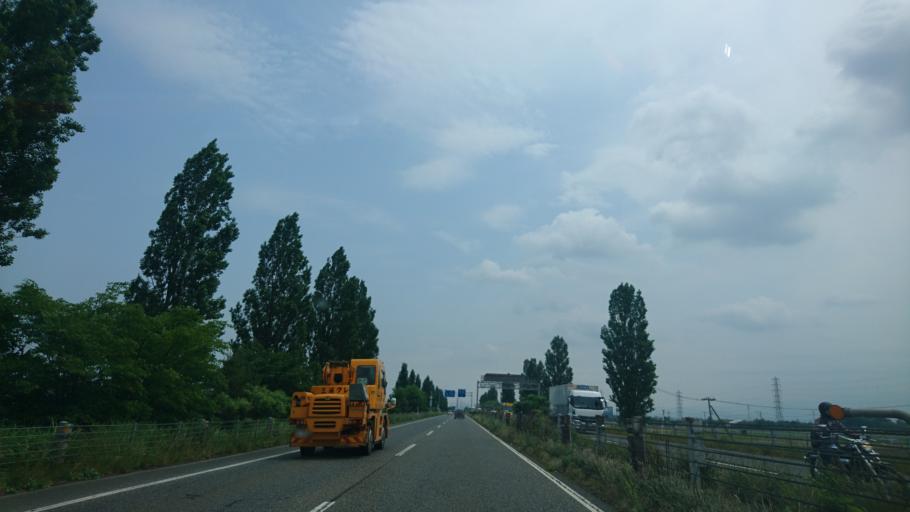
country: JP
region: Niigata
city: Kameda-honcho
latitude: 37.9382
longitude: 139.1740
